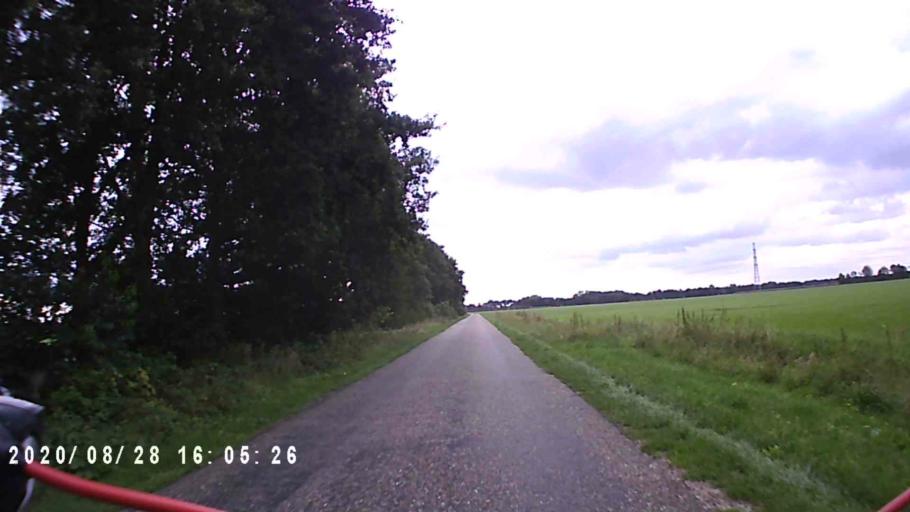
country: NL
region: Drenthe
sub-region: Gemeente Tynaarlo
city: Vries
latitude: 53.1156
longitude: 6.5017
